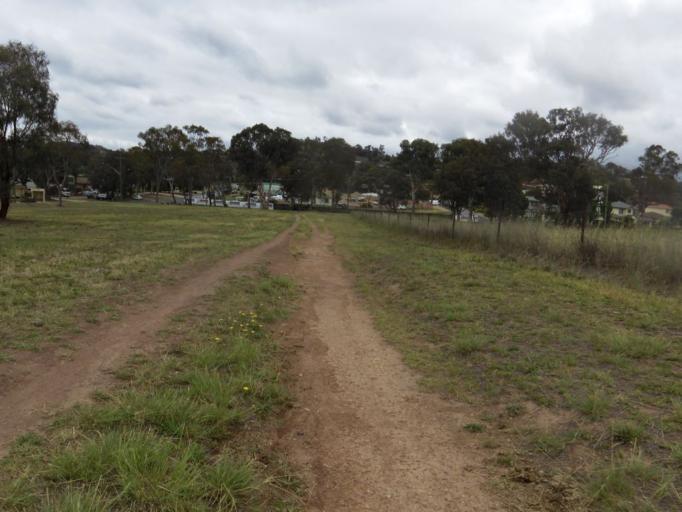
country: AU
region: Australian Capital Territory
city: Macquarie
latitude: -35.3457
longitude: 149.0279
